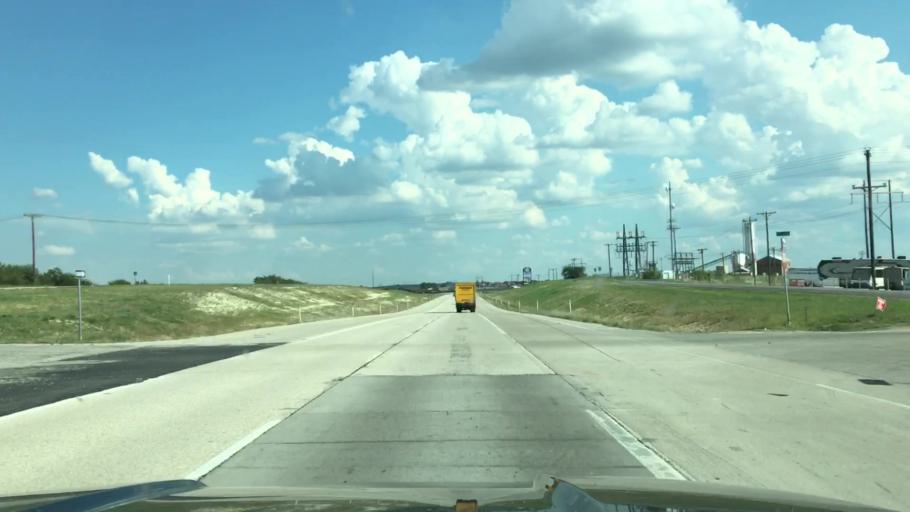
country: US
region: Texas
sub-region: Wise County
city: Decatur
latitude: 33.1802
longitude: -97.5480
